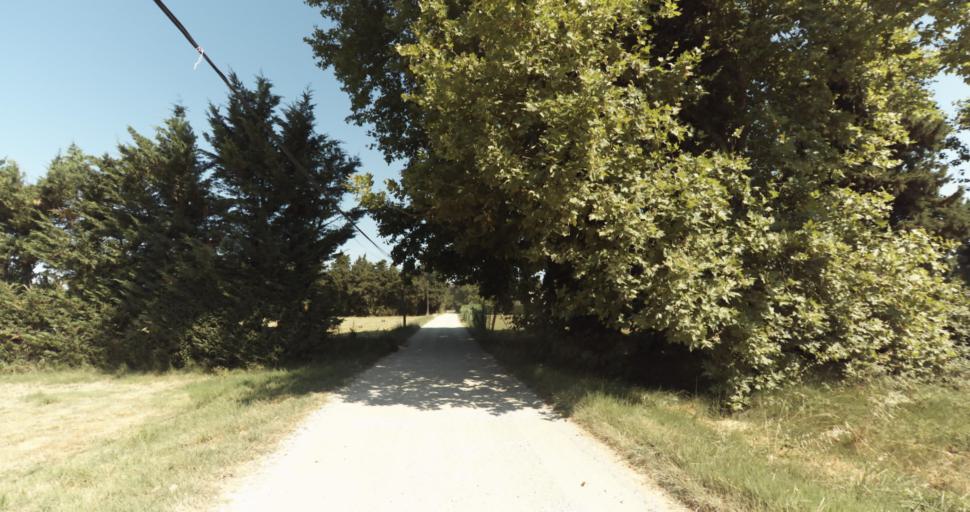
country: FR
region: Provence-Alpes-Cote d'Azur
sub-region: Departement du Vaucluse
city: Monteux
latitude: 44.0101
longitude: 5.0029
